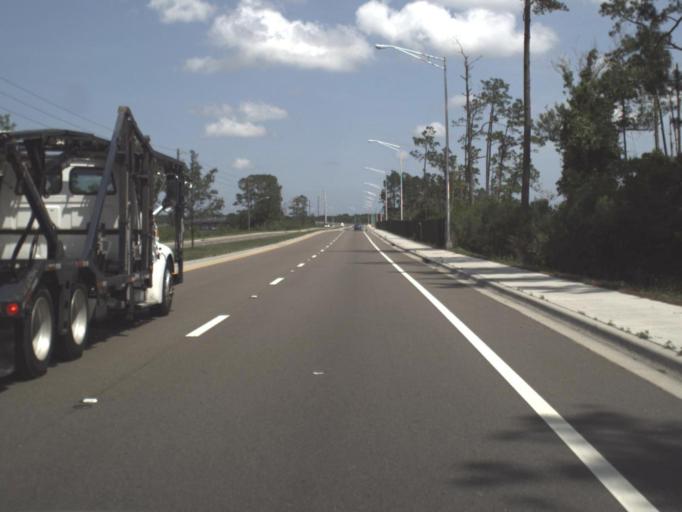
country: US
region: Florida
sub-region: Duval County
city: Jacksonville
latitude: 30.4151
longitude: -81.5922
